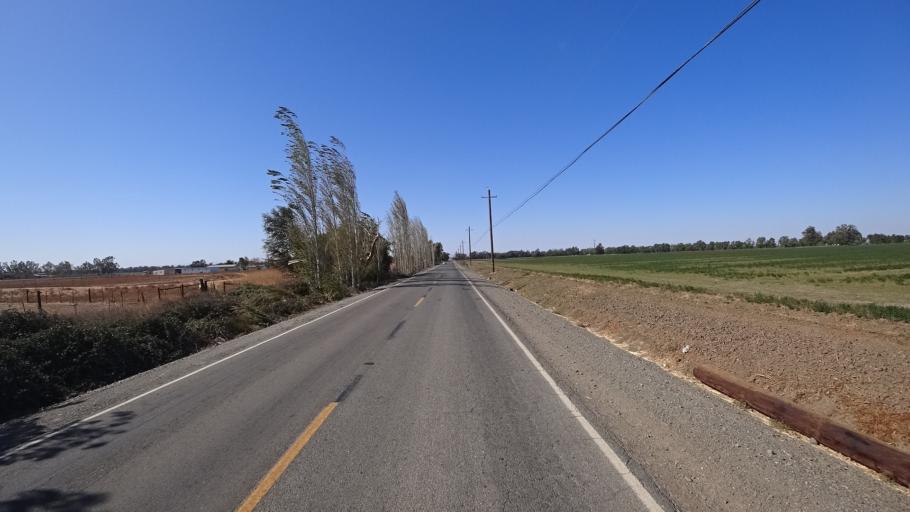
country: US
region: California
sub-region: Yolo County
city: Woodland
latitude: 38.6193
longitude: -121.7351
